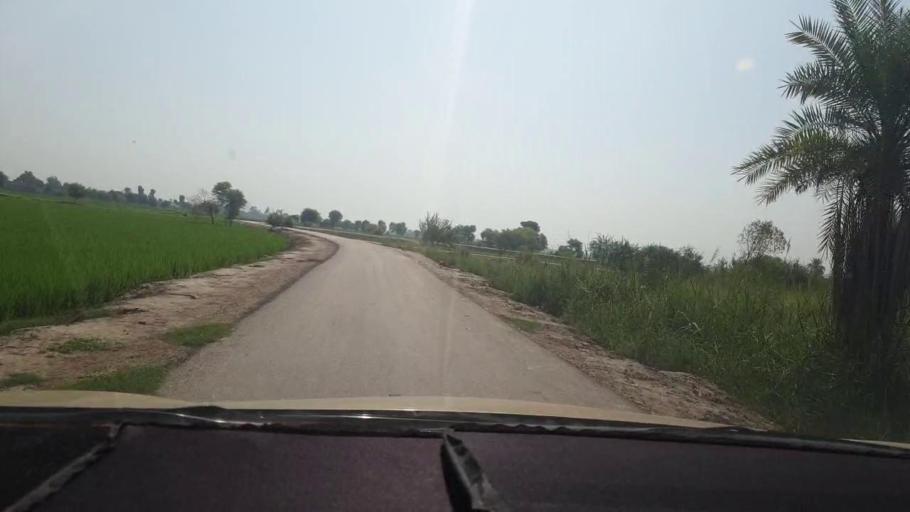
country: PK
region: Sindh
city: Kambar
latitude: 27.5724
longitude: 68.0424
